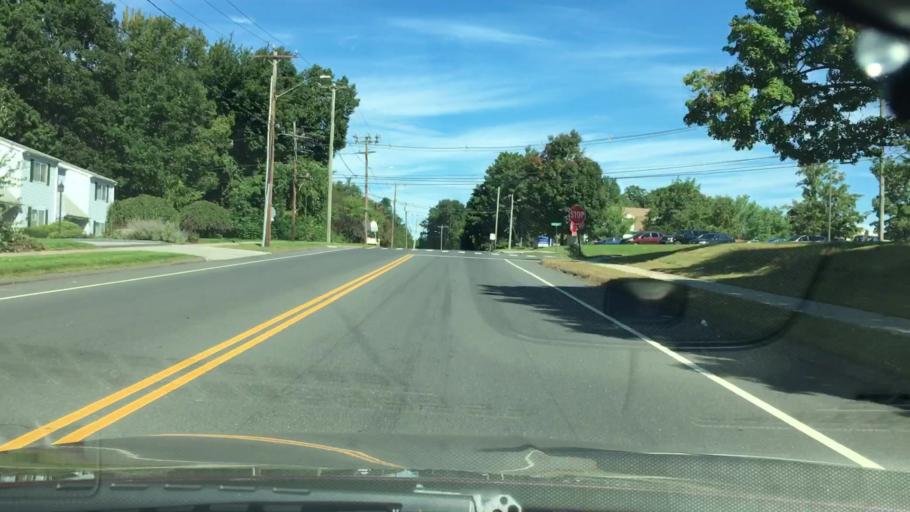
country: US
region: Connecticut
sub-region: Litchfield County
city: Terryville
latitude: 41.6847
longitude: -72.9842
